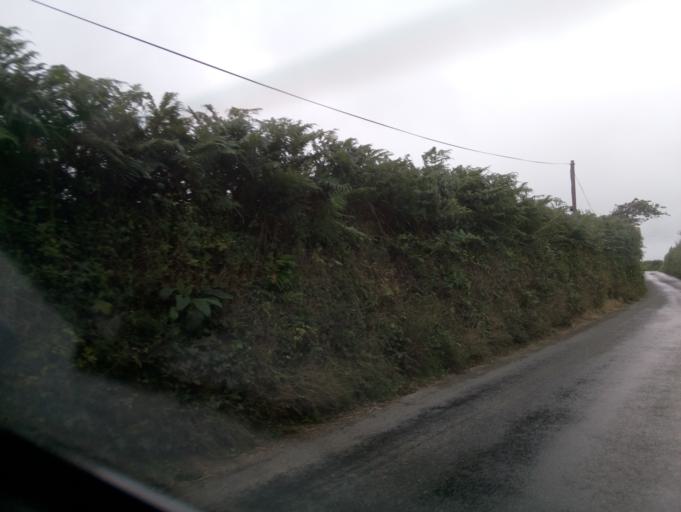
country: GB
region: England
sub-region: Devon
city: Kingsbridge
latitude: 50.3284
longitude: -3.7048
